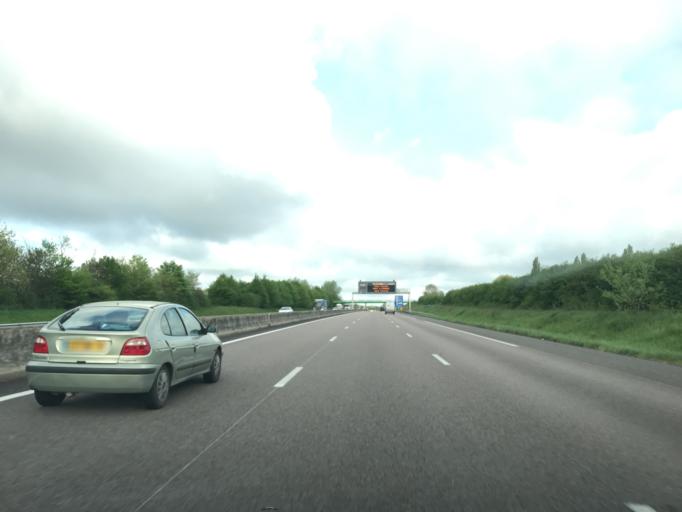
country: FR
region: Haute-Normandie
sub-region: Departement de l'Eure
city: Corneville-sur-Risle
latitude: 49.3732
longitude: 0.6570
